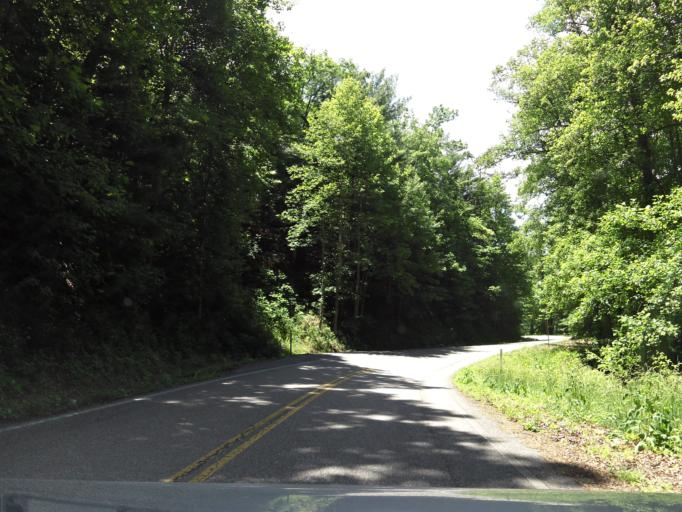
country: US
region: North Carolina
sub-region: Graham County
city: Robbinsville
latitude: 35.5010
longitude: -83.9483
